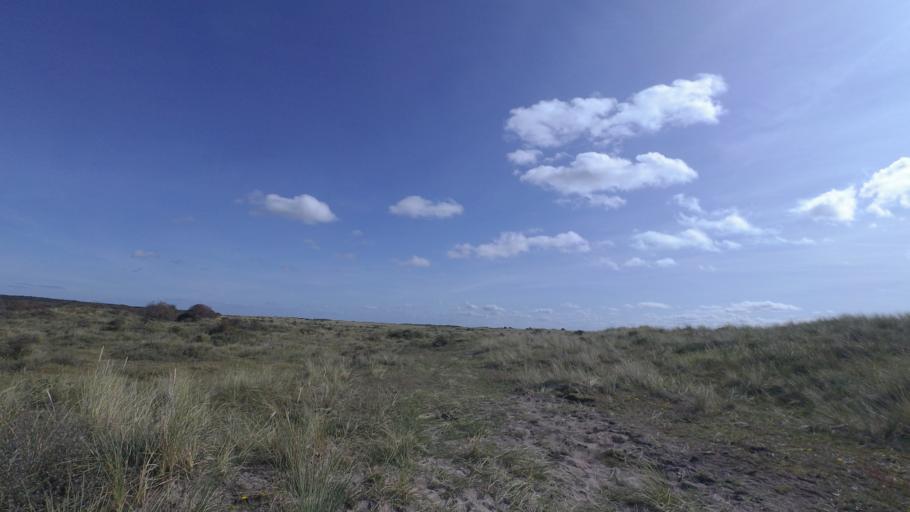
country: NL
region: Friesland
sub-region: Gemeente Ameland
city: Nes
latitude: 53.4512
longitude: 5.7322
